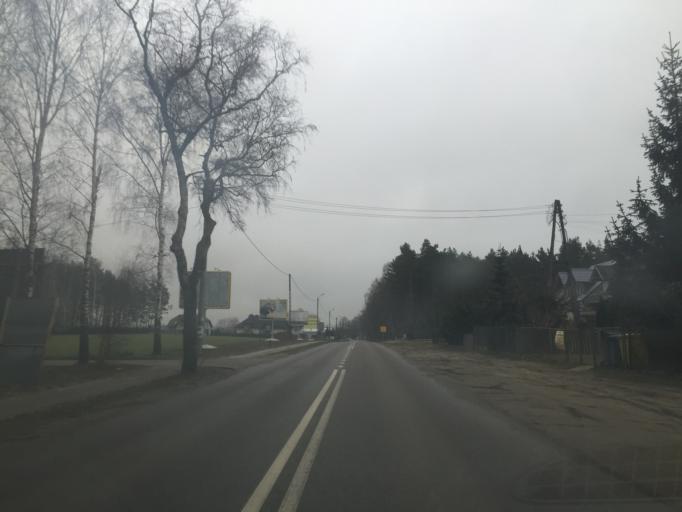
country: PL
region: Pomeranian Voivodeship
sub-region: Powiat kartuski
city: Banino
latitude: 54.3906
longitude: 18.4127
